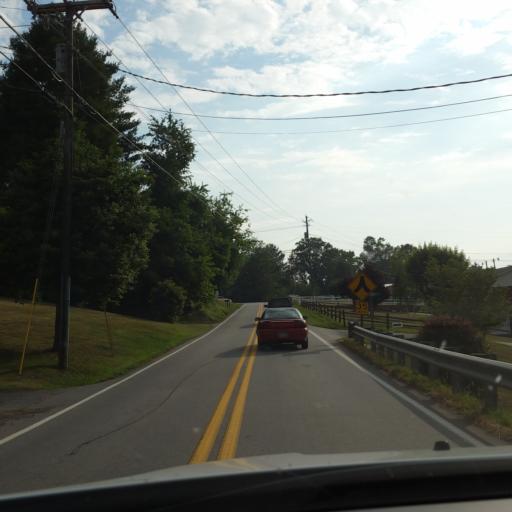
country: US
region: North Carolina
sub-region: Buncombe County
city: Bent Creek
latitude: 35.5298
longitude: -82.6735
